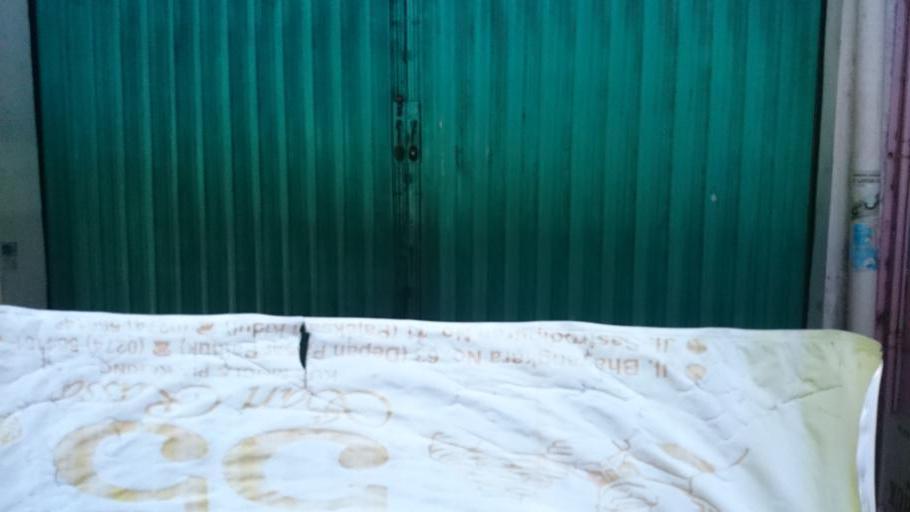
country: ID
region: Daerah Istimewa Yogyakarta
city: Yogyakarta
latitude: -7.7969
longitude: 110.3621
